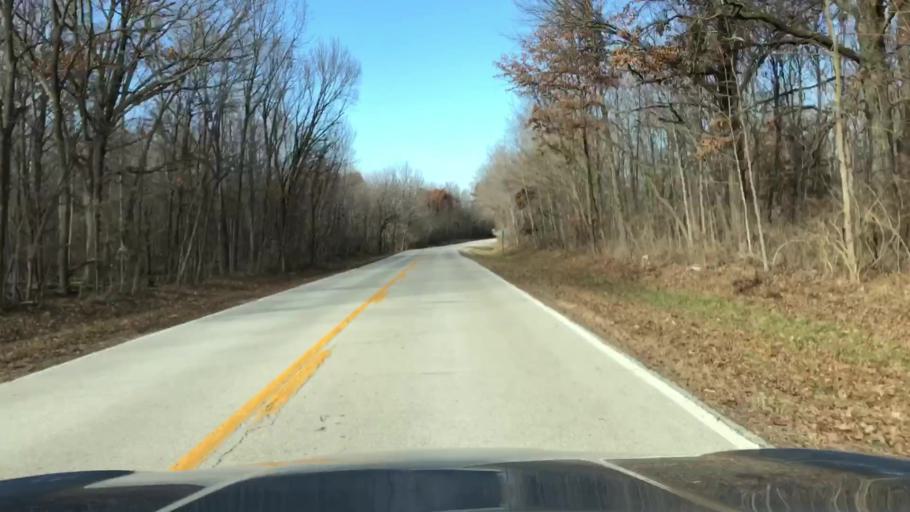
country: US
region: Illinois
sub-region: McLean County
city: Hudson
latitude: 40.6534
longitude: -88.9233
